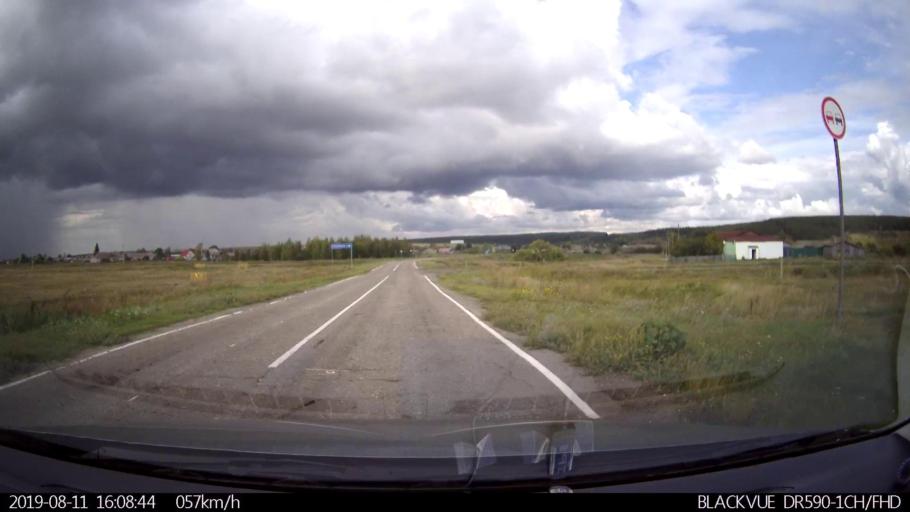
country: RU
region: Ulyanovsk
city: Ignatovka
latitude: 53.9873
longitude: 47.6491
